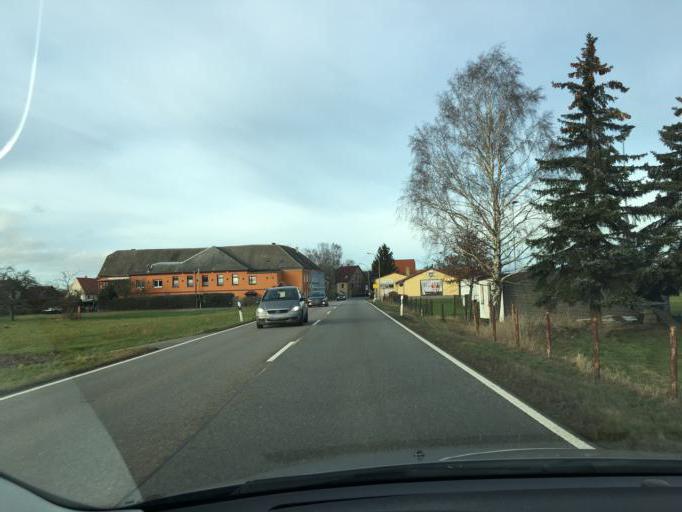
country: DE
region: Thuringia
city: Fockendorf
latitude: 51.0599
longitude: 12.4541
